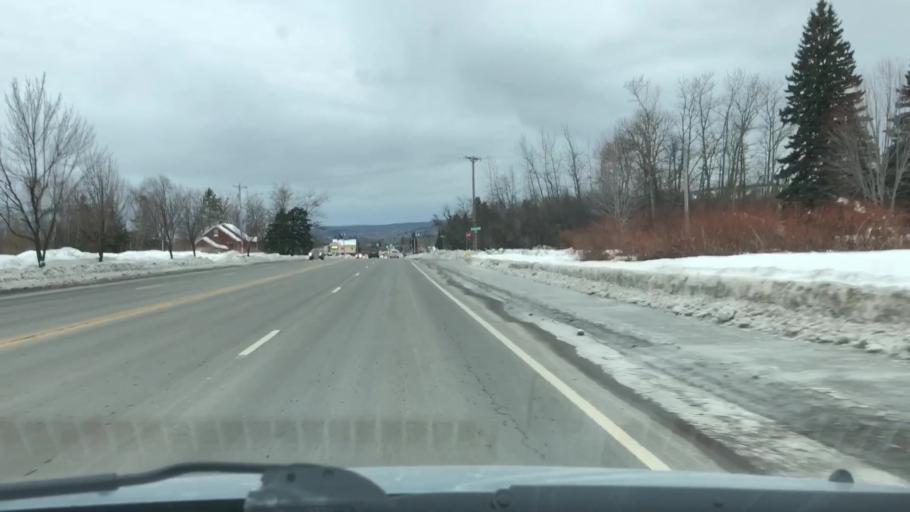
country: US
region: Minnesota
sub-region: Saint Louis County
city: Proctor
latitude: 46.7282
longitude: -92.1844
